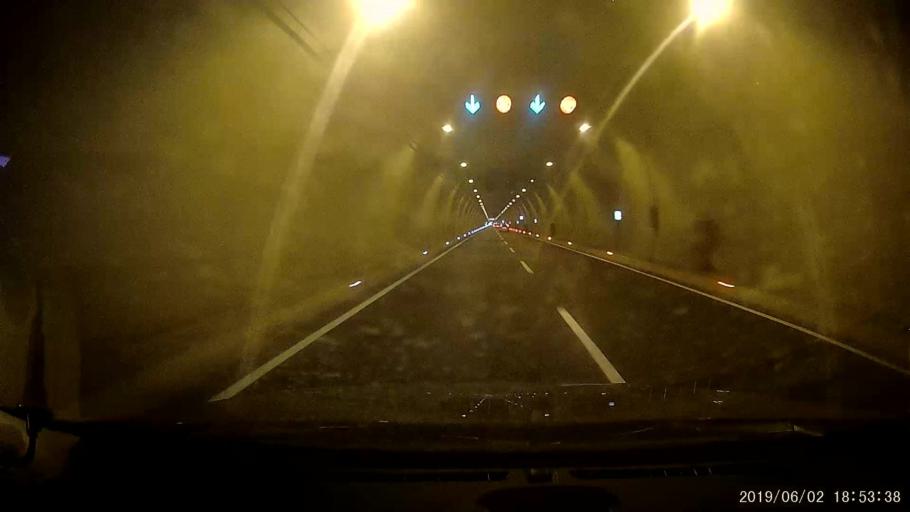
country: TR
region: Ordu
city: Ordu
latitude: 40.9766
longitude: 37.8349
